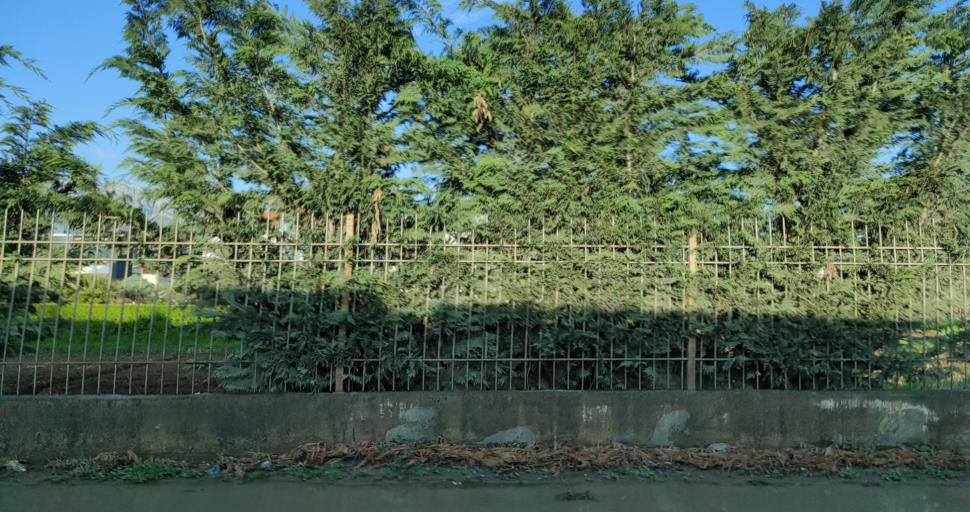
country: AL
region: Durres
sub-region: Rrethi i Krujes
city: Fushe-Kruje
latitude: 41.4784
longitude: 19.7348
